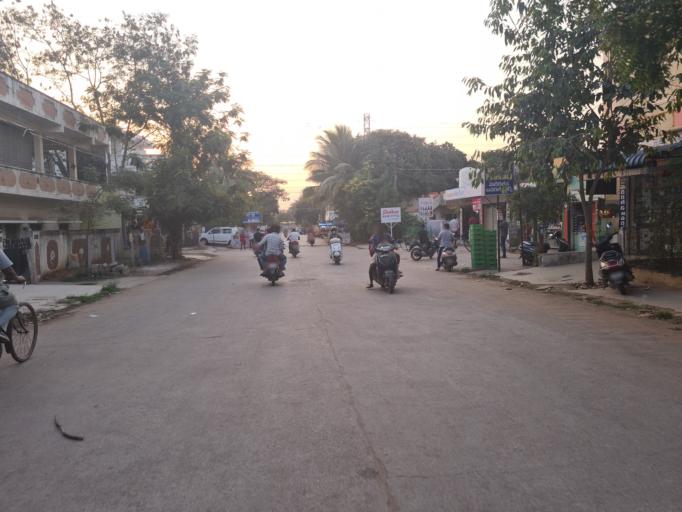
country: IN
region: Telangana
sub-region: Medak
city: Serilingampalle
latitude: 17.4778
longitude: 78.2846
